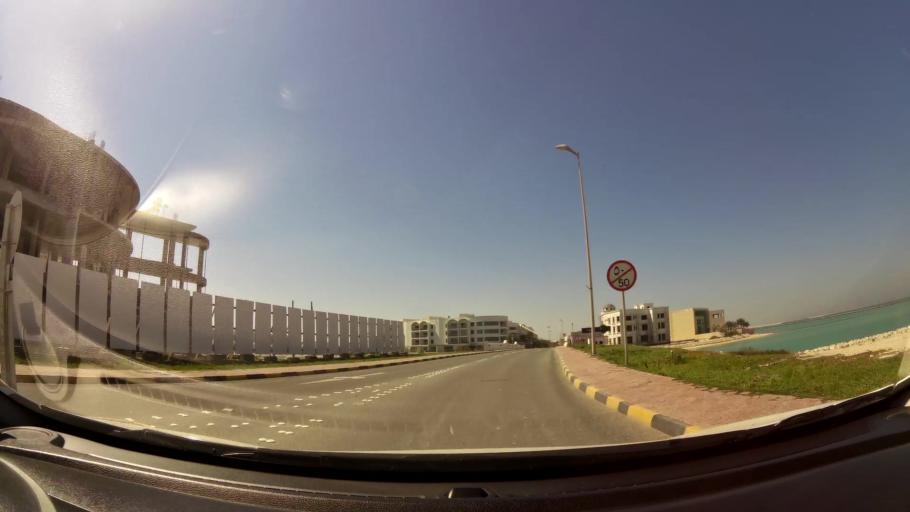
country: BH
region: Muharraq
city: Al Hadd
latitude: 26.2984
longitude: 50.6678
